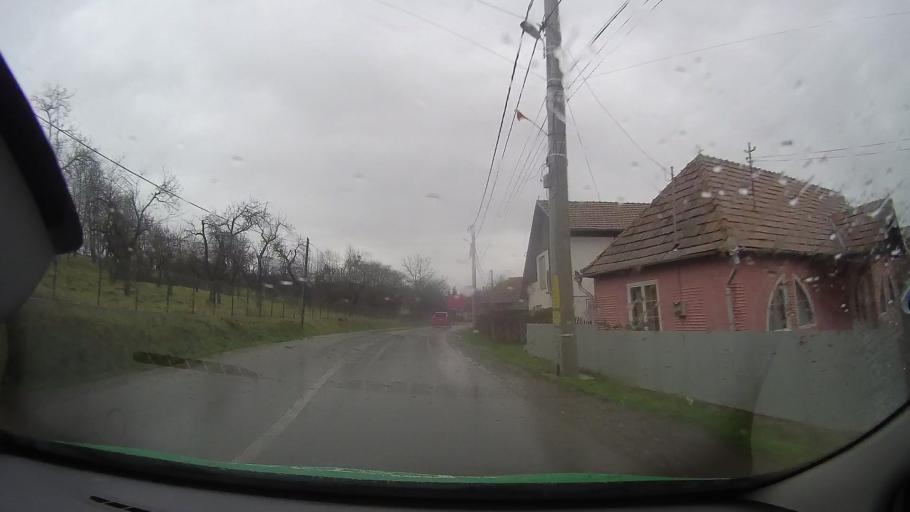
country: RO
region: Mures
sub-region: Comuna Vatava
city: Vatava
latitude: 46.9337
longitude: 24.7679
